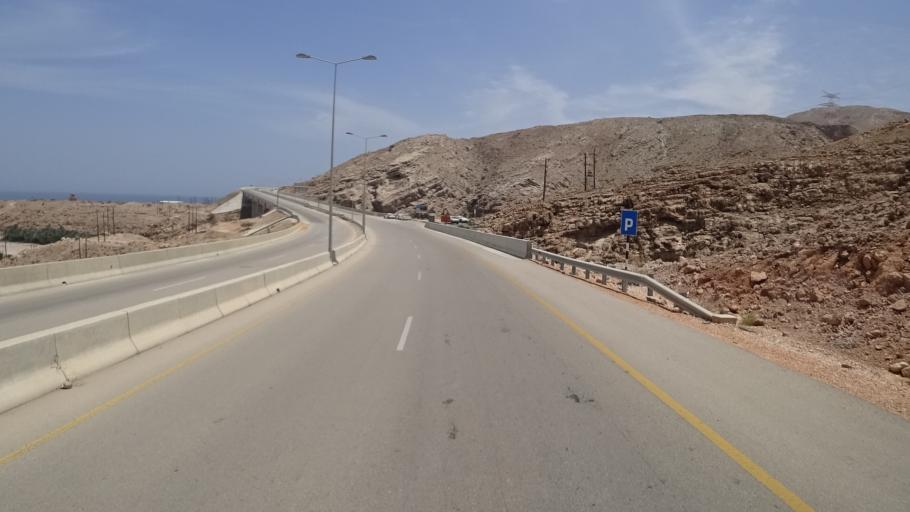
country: OM
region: Ash Sharqiyah
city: Sur
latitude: 22.6964
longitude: 59.3660
